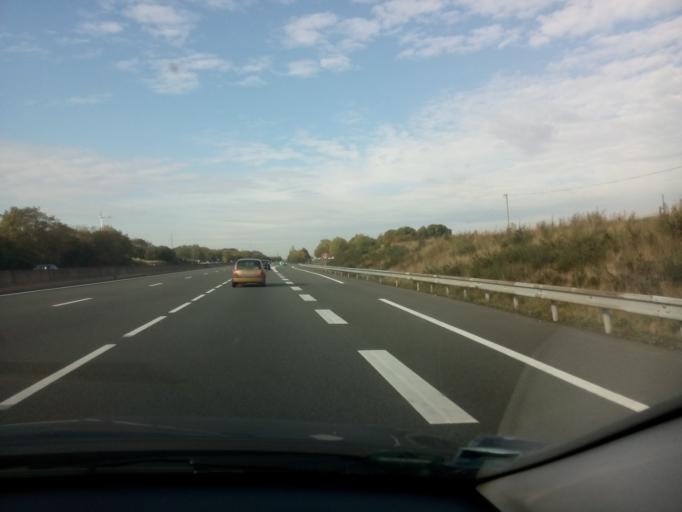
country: FR
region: Centre
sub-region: Departement d'Eure-et-Loir
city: Yevres
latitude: 48.2806
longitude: 1.2215
